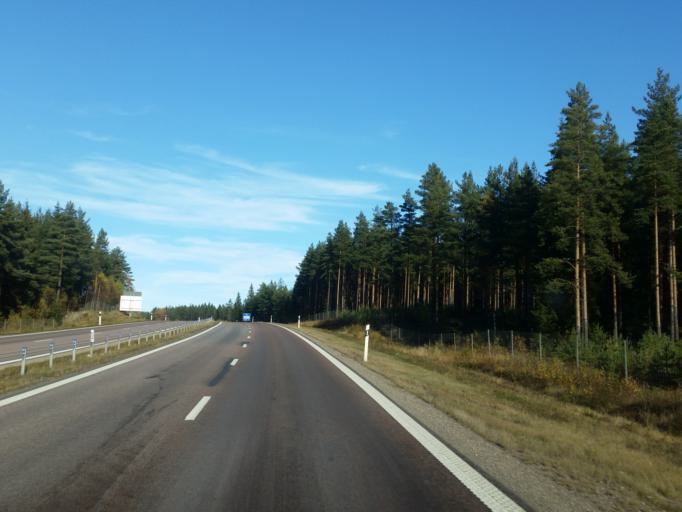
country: SE
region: Dalarna
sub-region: Borlange Kommun
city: Ornas
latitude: 60.5202
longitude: 15.5520
